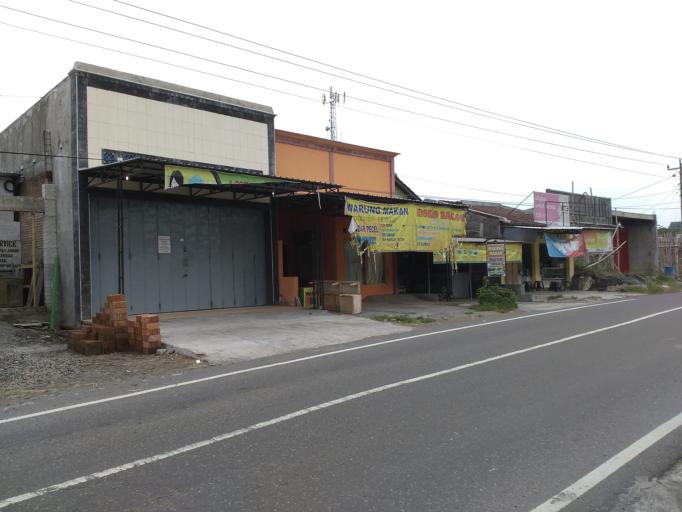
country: ID
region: Central Java
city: Boyolali
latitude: -7.5881
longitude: 110.6218
